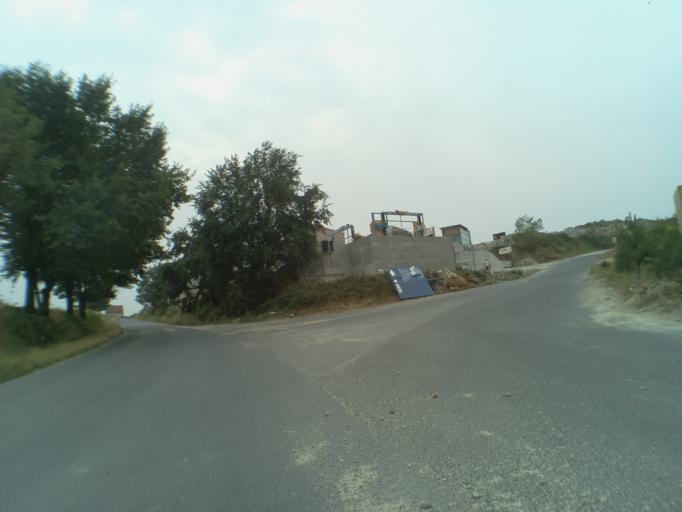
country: PL
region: Lower Silesian Voivodeship
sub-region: Powiat swidnicki
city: Strzegom
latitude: 50.9888
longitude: 16.2689
